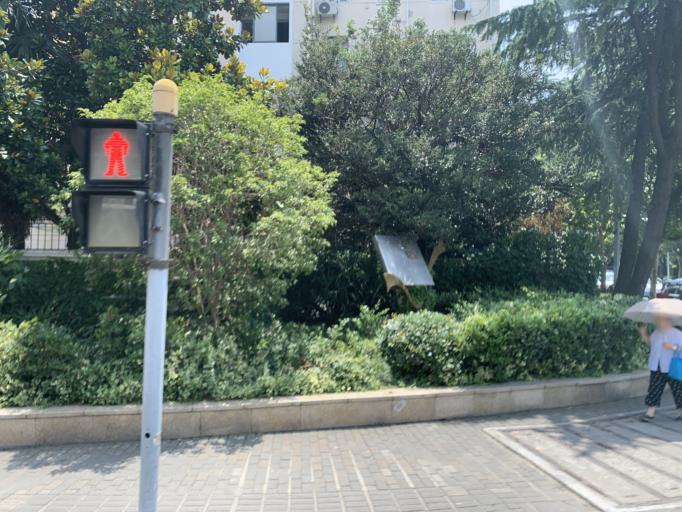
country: CN
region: Shanghai Shi
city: Pudong
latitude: 31.2377
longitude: 121.5182
